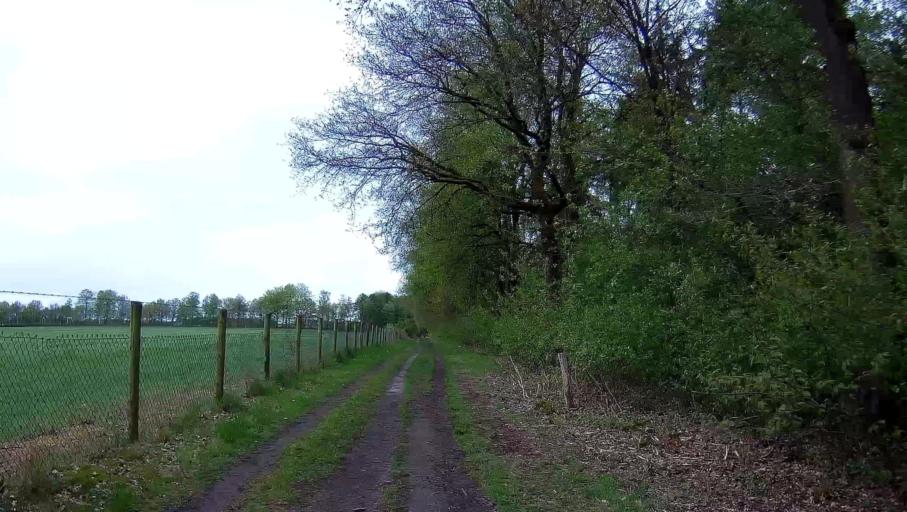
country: NL
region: Drenthe
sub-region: Gemeente Borger-Odoorn
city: Borger
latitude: 52.9422
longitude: 6.7751
